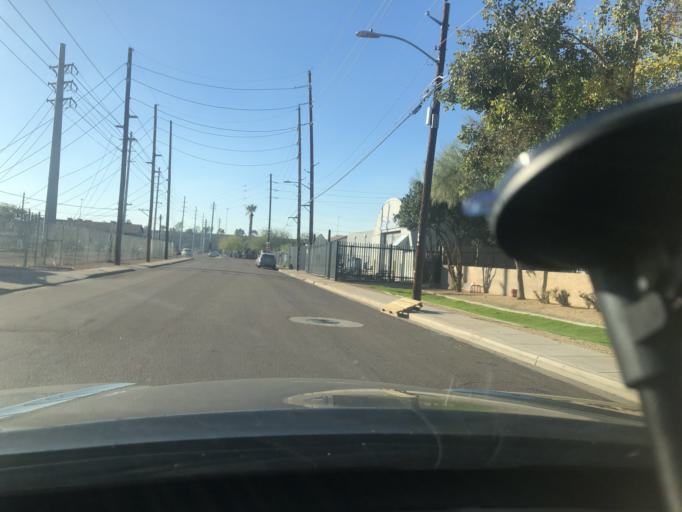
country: US
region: Arizona
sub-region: Maricopa County
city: Phoenix
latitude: 33.4530
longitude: -112.0314
